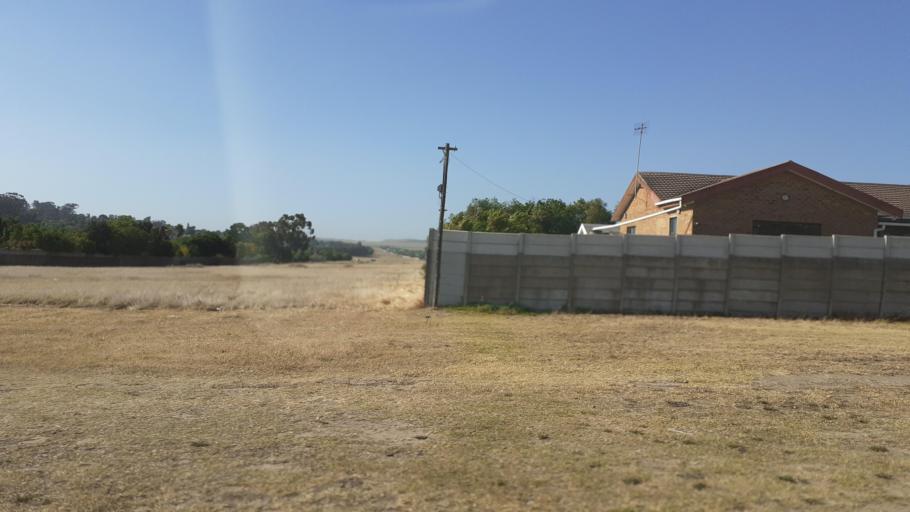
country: ZA
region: Western Cape
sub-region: City of Cape Town
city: Kraaifontein
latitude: -33.8259
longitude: 18.6708
